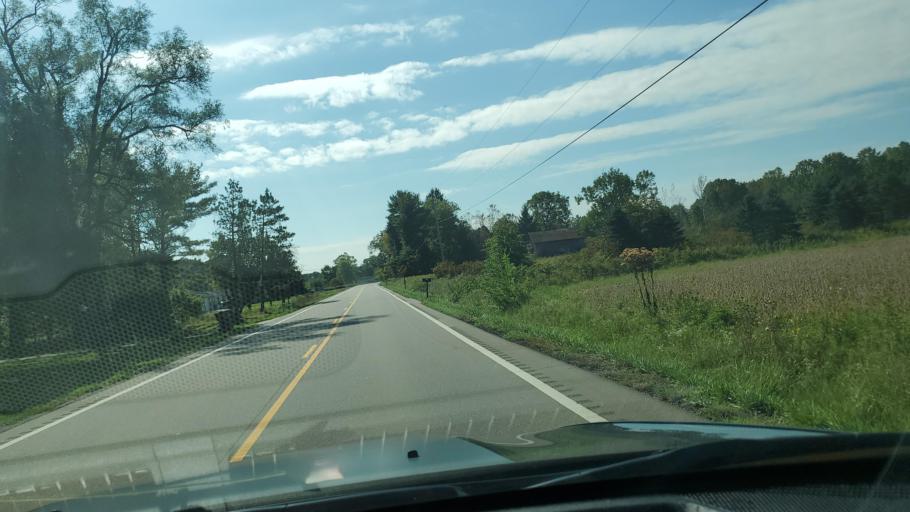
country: US
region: Ohio
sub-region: Trumbull County
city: Cortland
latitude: 41.4254
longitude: -80.6007
